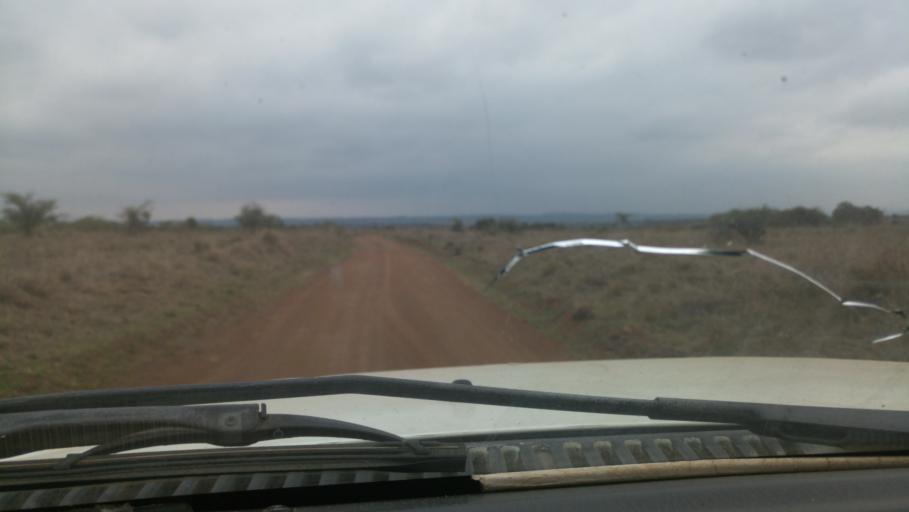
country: KE
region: Nairobi Area
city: Pumwani
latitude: -1.3825
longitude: 36.8411
